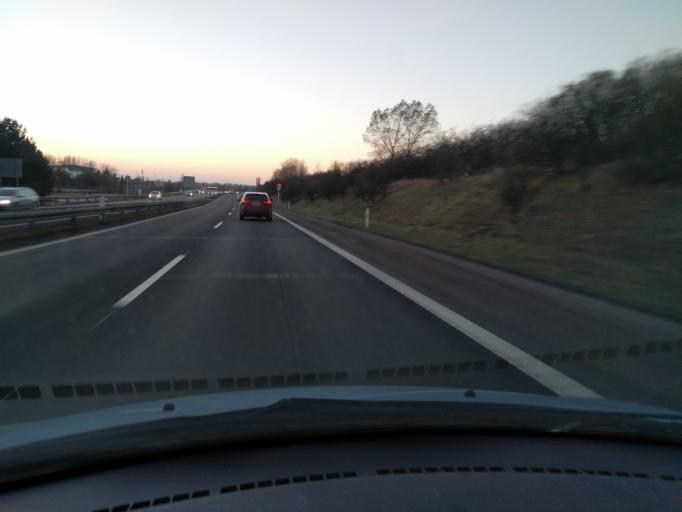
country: DK
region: South Denmark
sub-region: Nyborg Kommune
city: Nyborg
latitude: 55.3050
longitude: 10.8224
